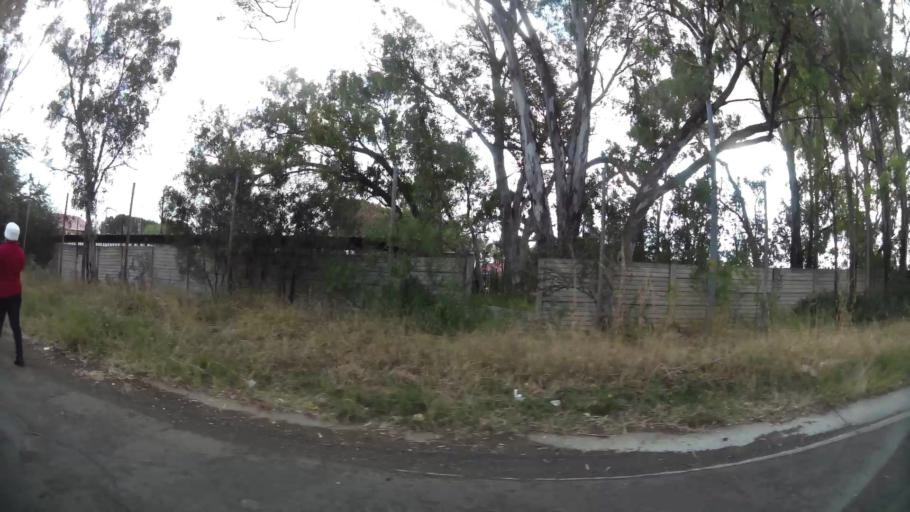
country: ZA
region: Orange Free State
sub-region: Mangaung Metropolitan Municipality
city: Bloemfontein
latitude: -29.0811
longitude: 26.1960
